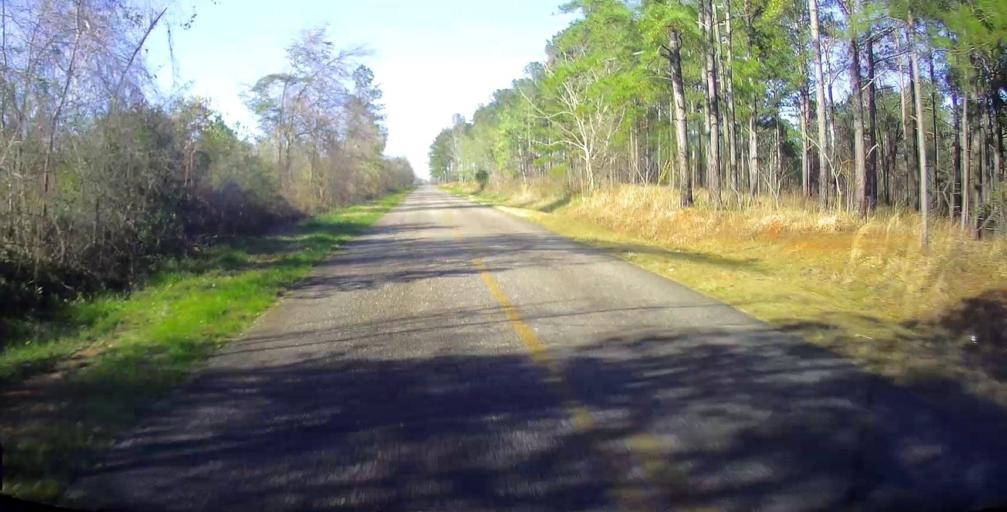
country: US
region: Georgia
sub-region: Macon County
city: Marshallville
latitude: 32.4783
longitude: -83.9522
